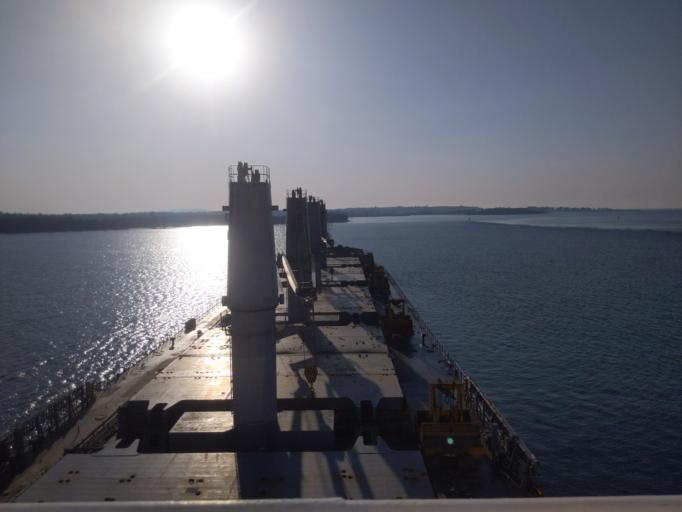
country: ZA
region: KwaZulu-Natal
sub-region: uThungulu District Municipality
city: Richards Bay
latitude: -28.8017
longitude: 32.0556
